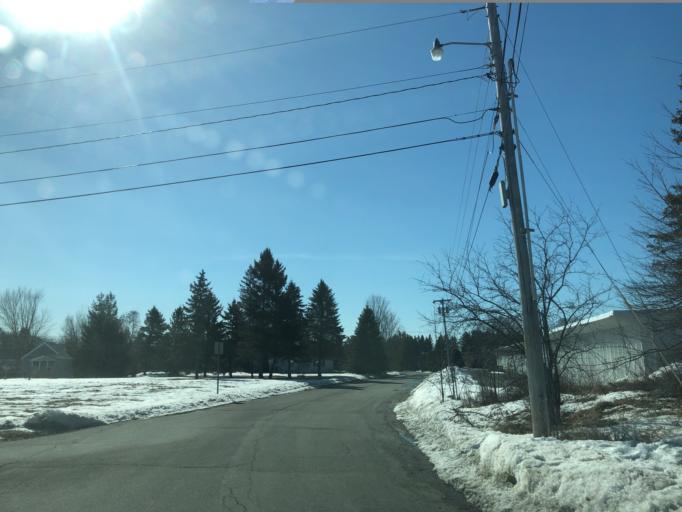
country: US
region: Maine
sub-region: Penobscot County
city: Brewer
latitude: 44.8187
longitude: -68.7523
